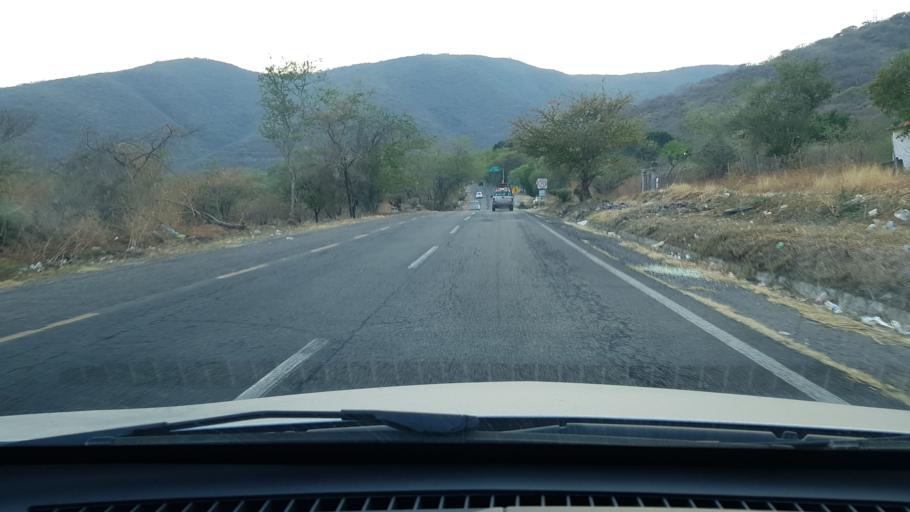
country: MX
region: Morelos
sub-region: Jiutepec
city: Independencia
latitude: 18.8587
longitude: -99.1057
